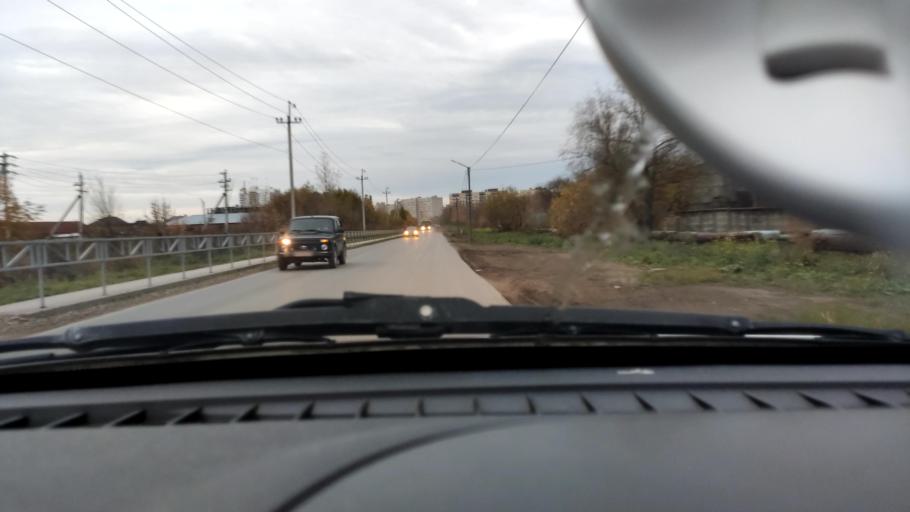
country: RU
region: Perm
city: Kondratovo
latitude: 57.9837
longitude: 56.1162
